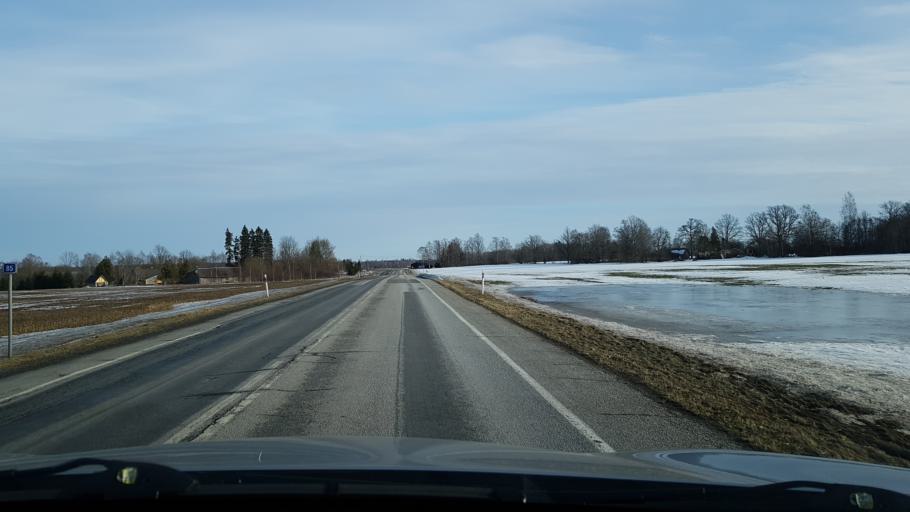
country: EE
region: Viljandimaa
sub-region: Viljandi linn
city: Viljandi
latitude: 58.3559
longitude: 25.4329
